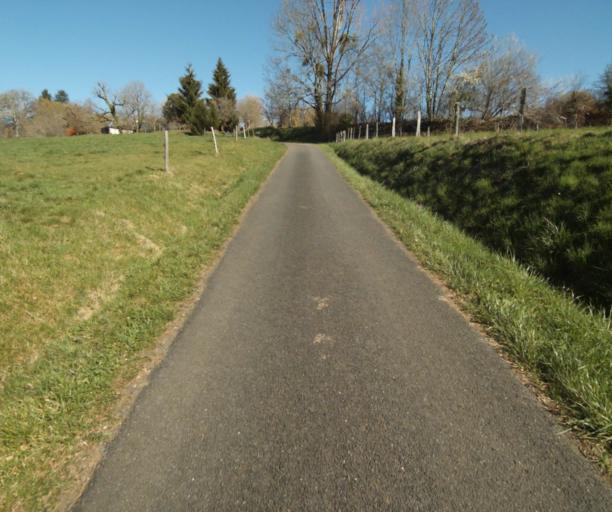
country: FR
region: Limousin
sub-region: Departement de la Correze
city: Seilhac
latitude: 45.3846
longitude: 1.7511
